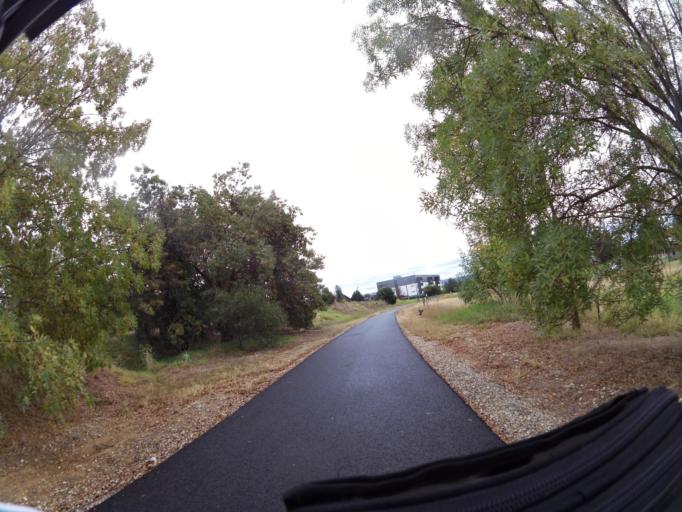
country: AU
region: Victoria
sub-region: Wodonga
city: Wodonga
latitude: -36.1240
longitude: 146.8932
